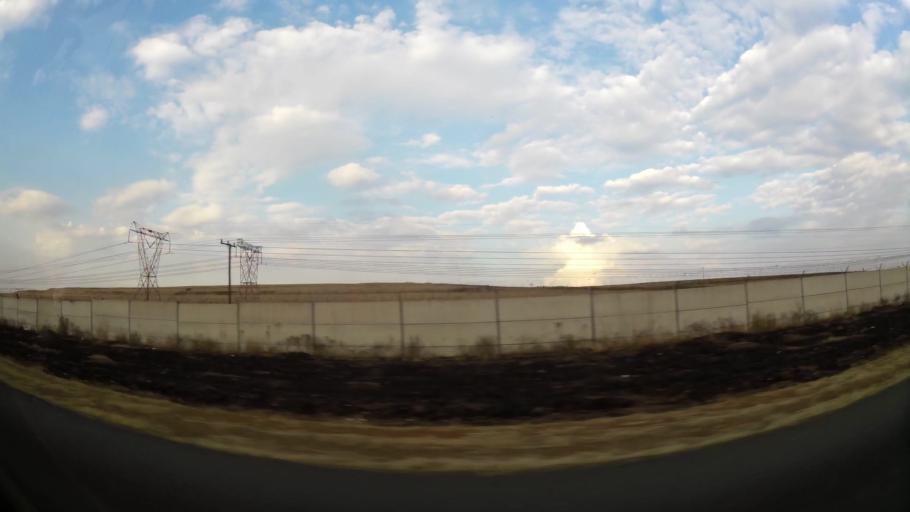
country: ZA
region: Gauteng
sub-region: Sedibeng District Municipality
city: Vanderbijlpark
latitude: -26.6392
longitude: 27.8062
